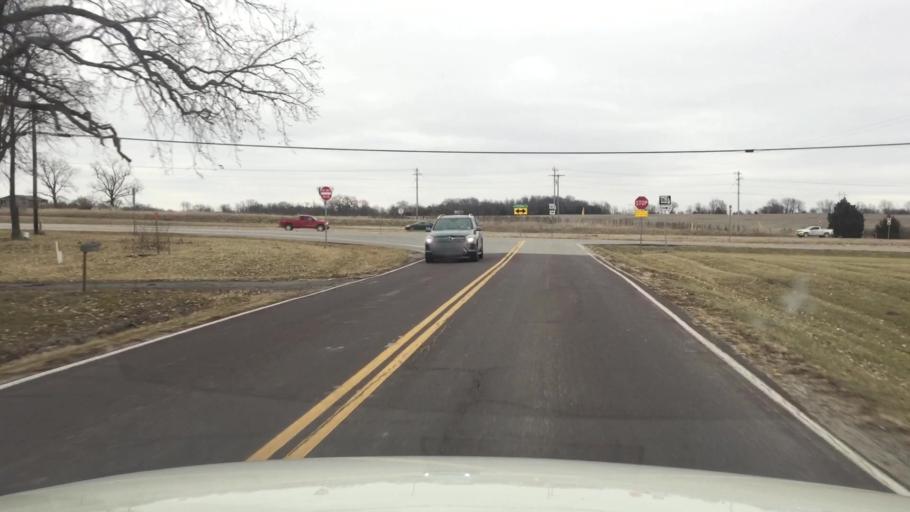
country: US
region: Missouri
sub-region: Boone County
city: Ashland
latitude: 38.8687
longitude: -92.2529
